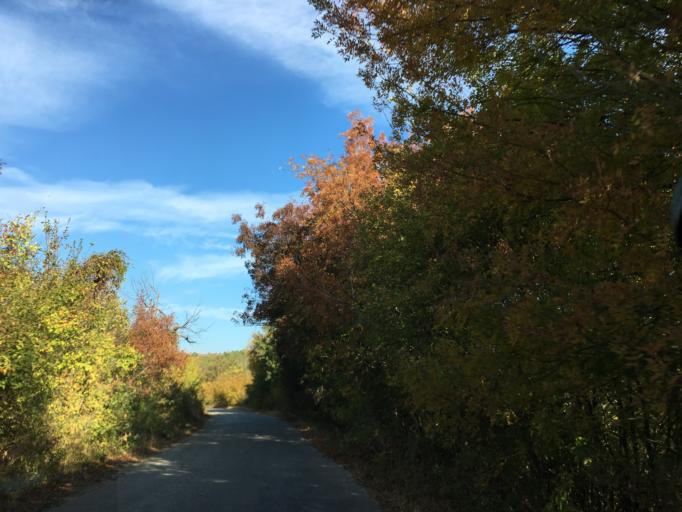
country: BG
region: Khaskovo
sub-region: Obshtina Ivaylovgrad
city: Ivaylovgrad
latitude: 41.3991
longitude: 26.1262
